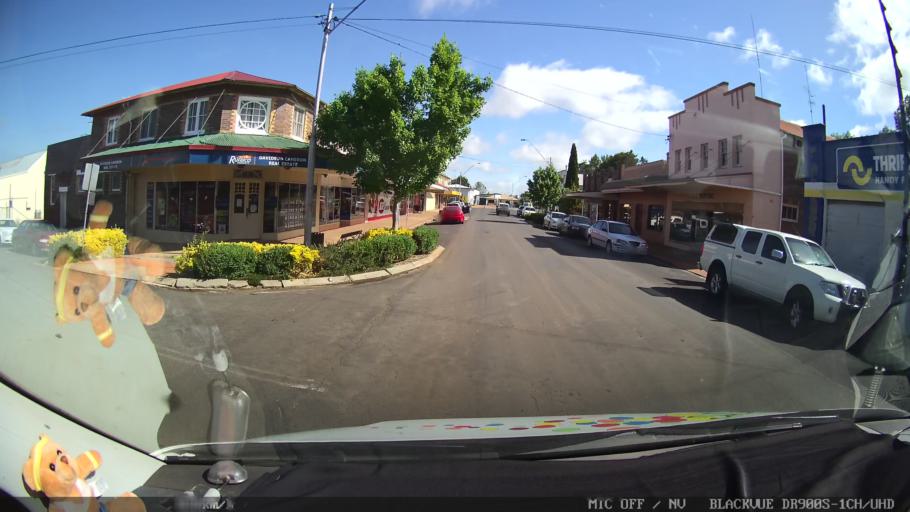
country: AU
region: New South Wales
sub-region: Guyra
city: Guyra
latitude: -30.2181
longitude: 151.6719
